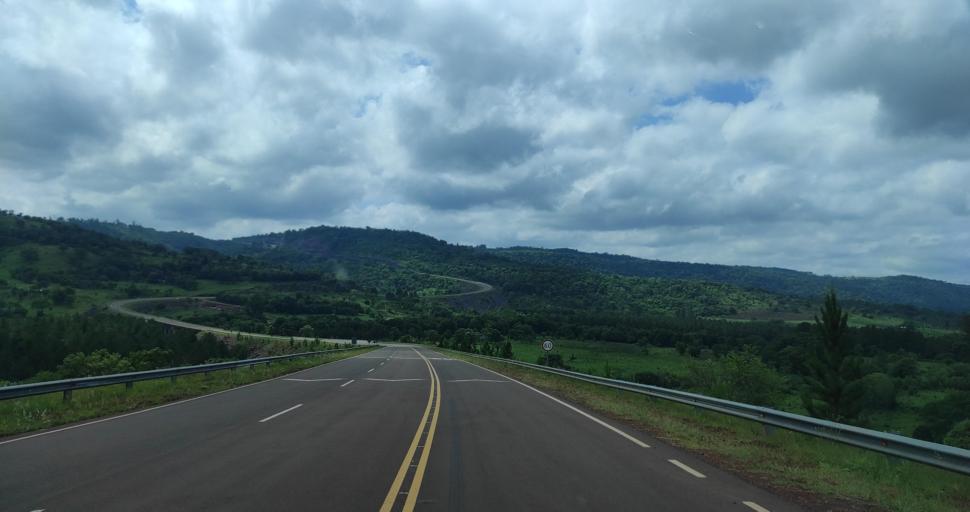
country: AR
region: Misiones
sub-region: Departamento de Veinticinco de Mayo
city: Veinticinco de Mayo
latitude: -27.3770
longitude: -54.8285
